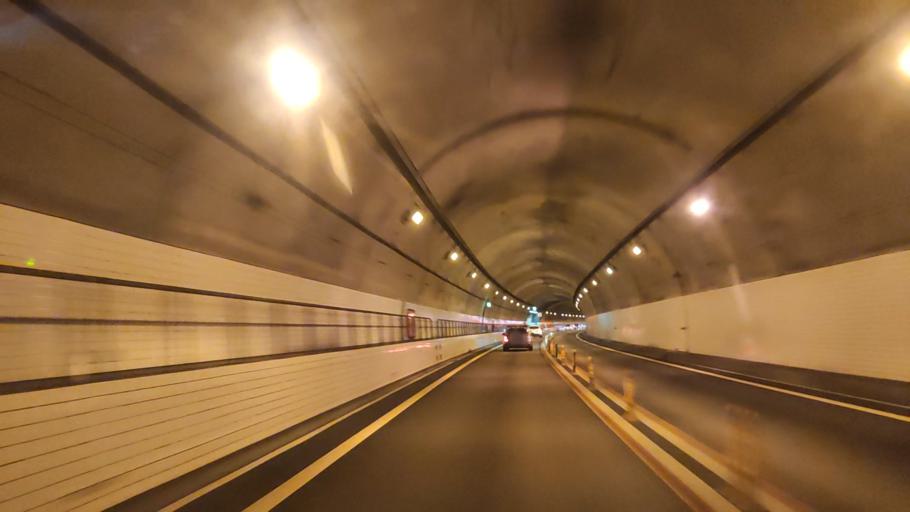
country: JP
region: Tokushima
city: Ikedacho
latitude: 34.0202
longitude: 133.8109
